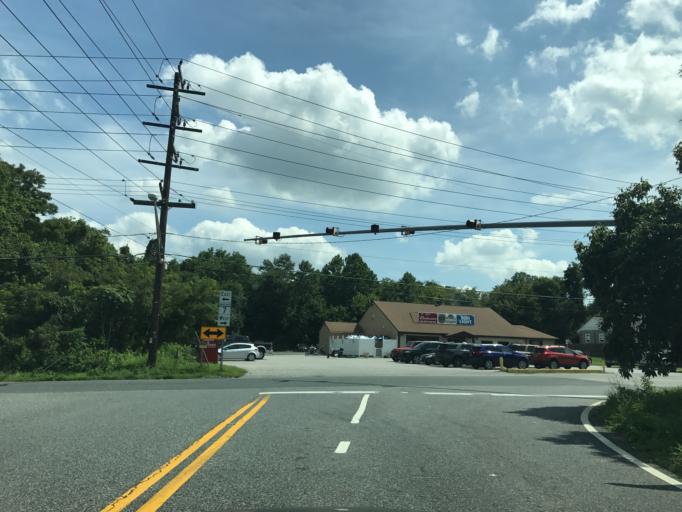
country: US
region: Maryland
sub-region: Harford County
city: Riverside
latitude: 39.4740
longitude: -76.2643
